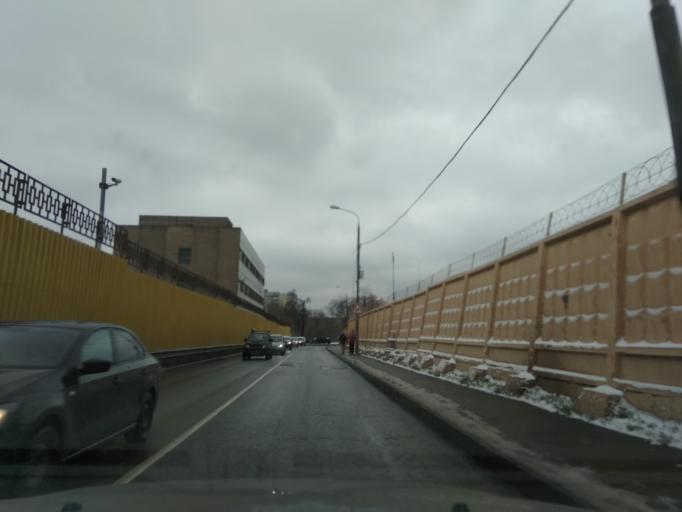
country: RU
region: Moskovskaya
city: Khoroshevo-Mnevniki
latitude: 55.7927
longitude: 37.4654
